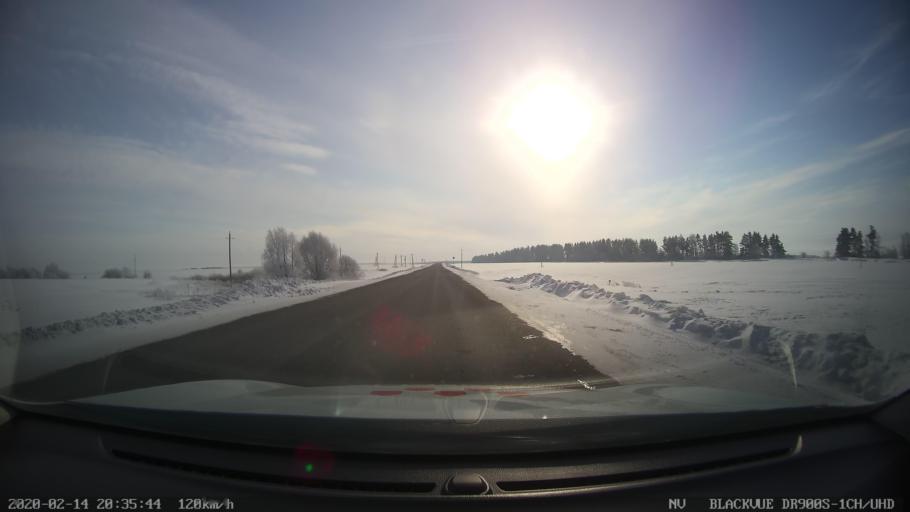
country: RU
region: Tatarstan
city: Kuybyshevskiy Zaton
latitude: 55.3781
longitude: 48.9894
